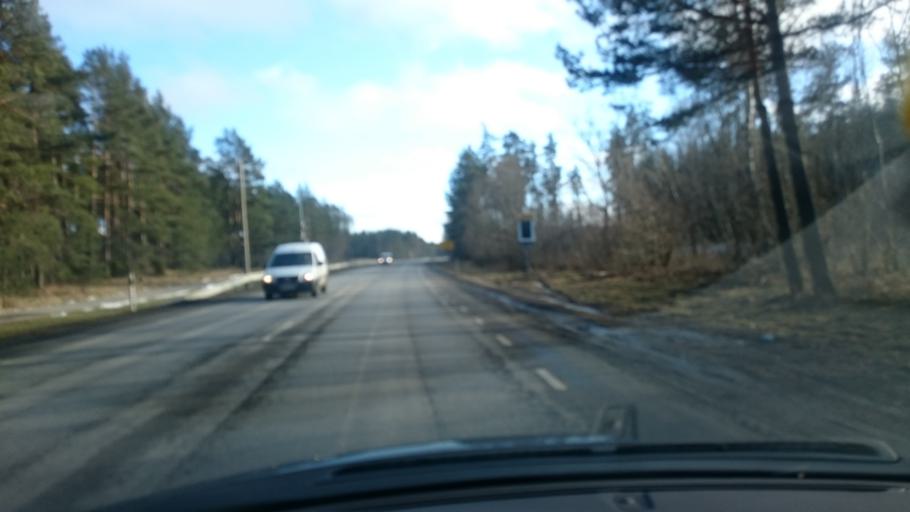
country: EE
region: Harju
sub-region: Tallinna linn
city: Tallinn
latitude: 59.3598
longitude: 24.7676
